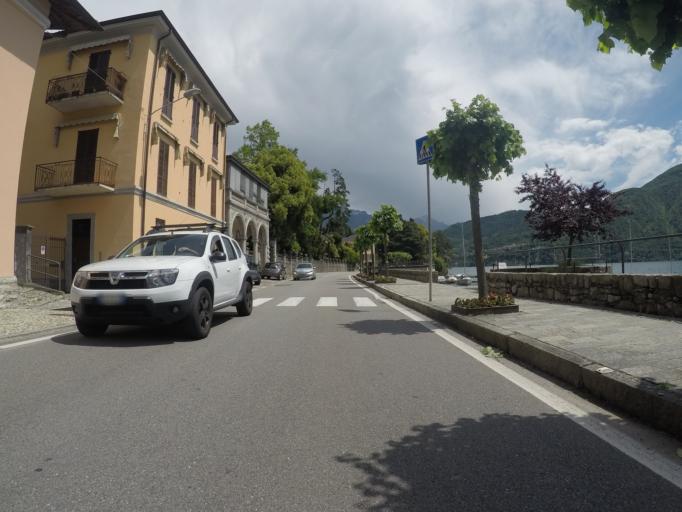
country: IT
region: Lombardy
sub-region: Provincia di Como
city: Tremezzo
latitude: 45.9823
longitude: 9.2179
